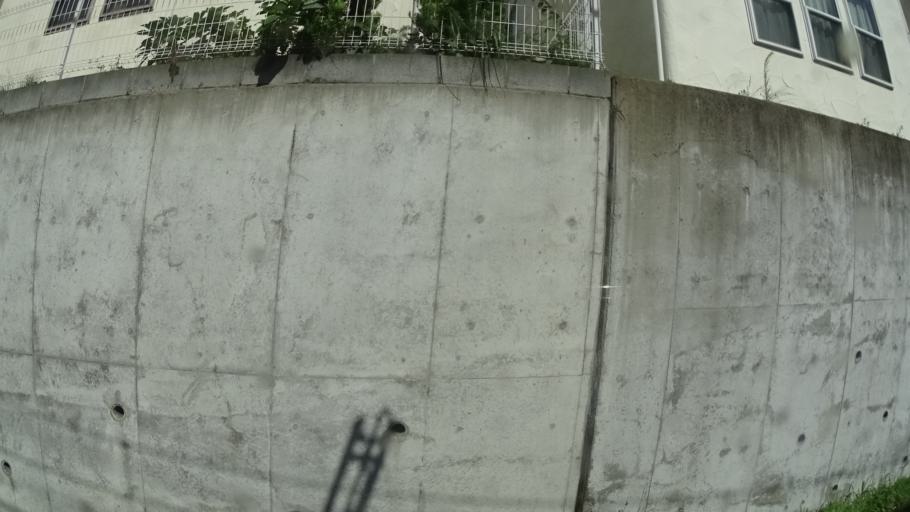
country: JP
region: Kanagawa
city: Fujisawa
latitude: 35.3236
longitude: 139.4836
